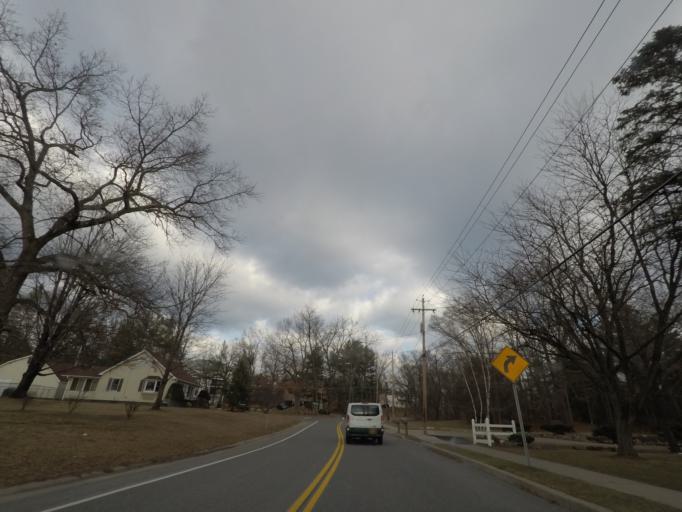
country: US
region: New York
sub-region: Albany County
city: Westmere
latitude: 42.6841
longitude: -73.8712
